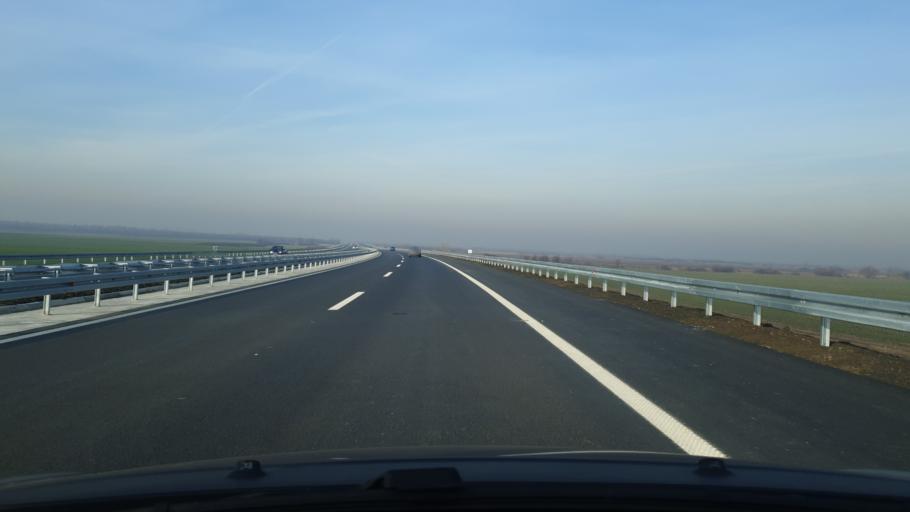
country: RS
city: Umka
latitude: 44.6915
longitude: 20.2673
